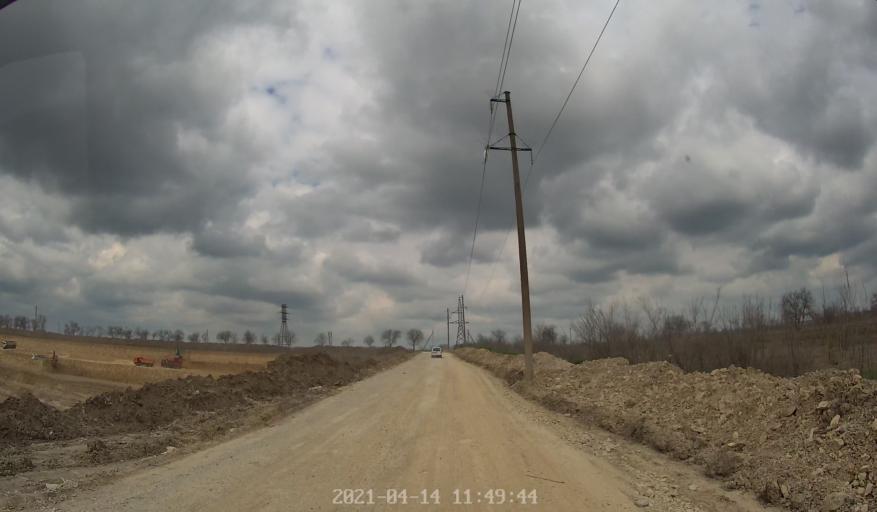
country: MD
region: Criuleni
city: Criuleni
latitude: 47.1672
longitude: 29.1847
